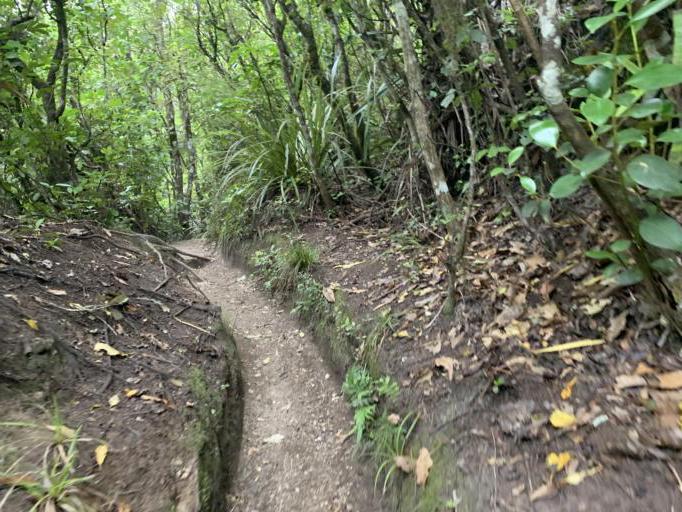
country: NZ
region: Waikato
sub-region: Taupo District
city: Taupo
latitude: -38.6977
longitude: 176.1512
